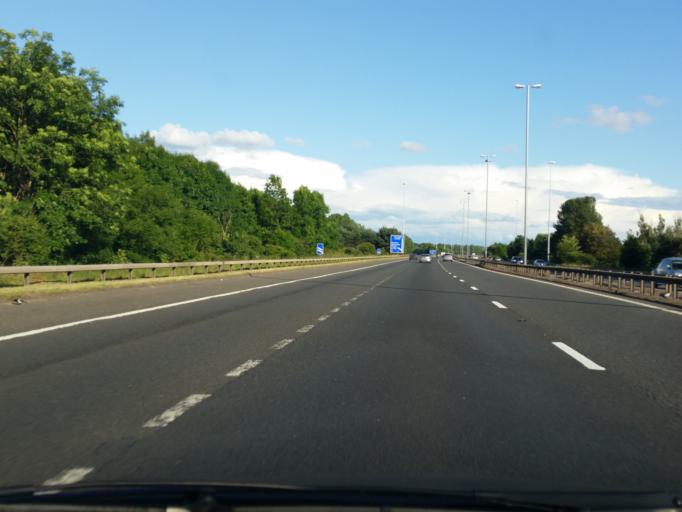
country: GB
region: Scotland
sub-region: South Lanarkshire
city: Hamilton
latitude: 55.7867
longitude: -4.0309
